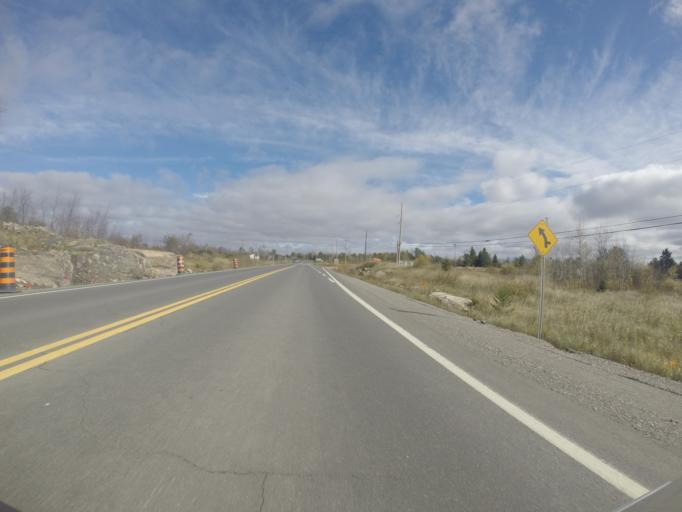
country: CA
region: Ontario
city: Greater Sudbury
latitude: 46.1046
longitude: -80.6616
